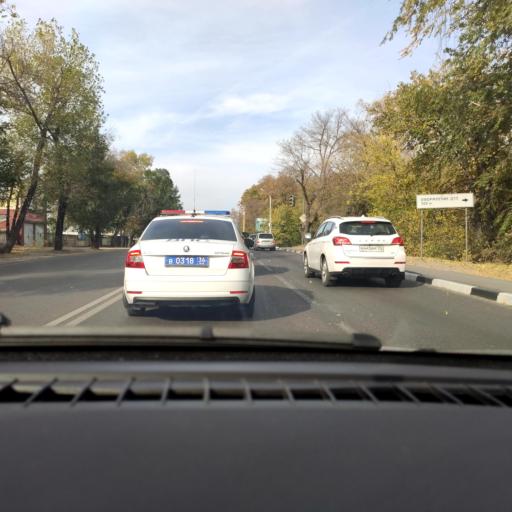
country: RU
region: Voronezj
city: Voronezh
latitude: 51.6675
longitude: 39.2712
